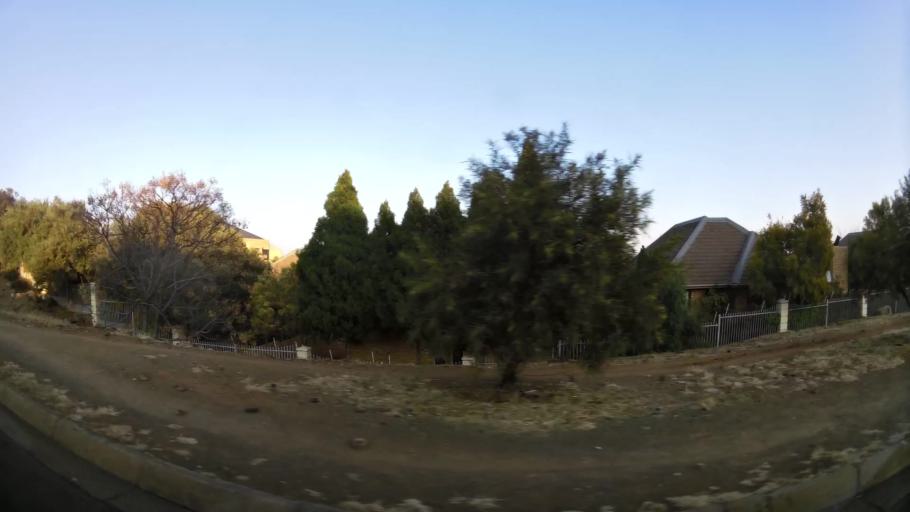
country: ZA
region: Orange Free State
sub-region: Mangaung Metropolitan Municipality
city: Bloemfontein
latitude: -29.0892
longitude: 26.1641
